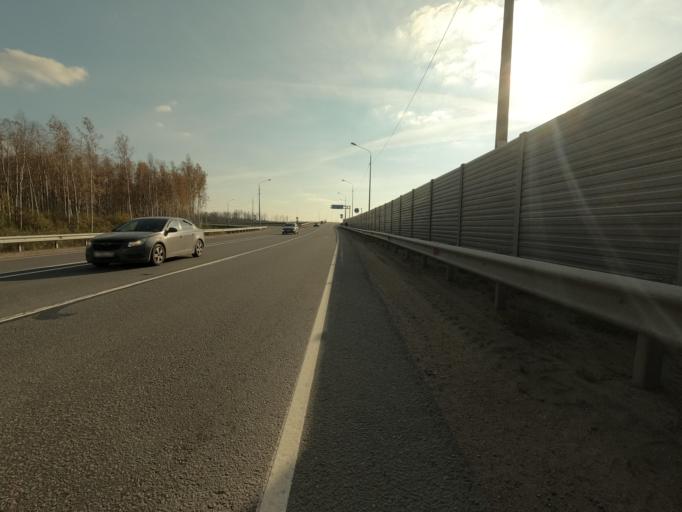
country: RU
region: Leningrad
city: Mga
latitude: 59.7606
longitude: 31.0936
